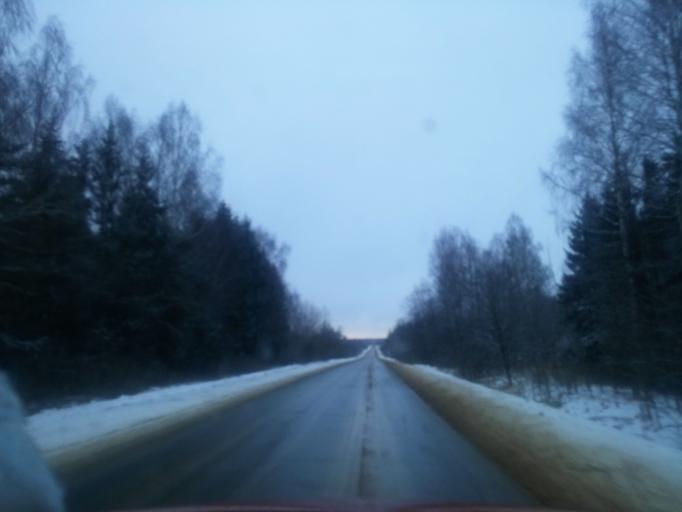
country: RU
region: Tverskaya
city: Likhoslavl'
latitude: 57.0007
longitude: 35.4510
